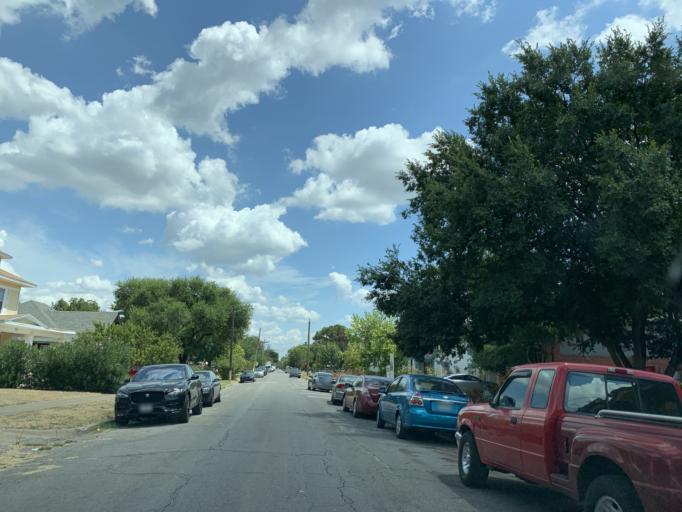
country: US
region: Texas
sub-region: Dallas County
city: Dallas
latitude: 32.7464
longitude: -96.8353
